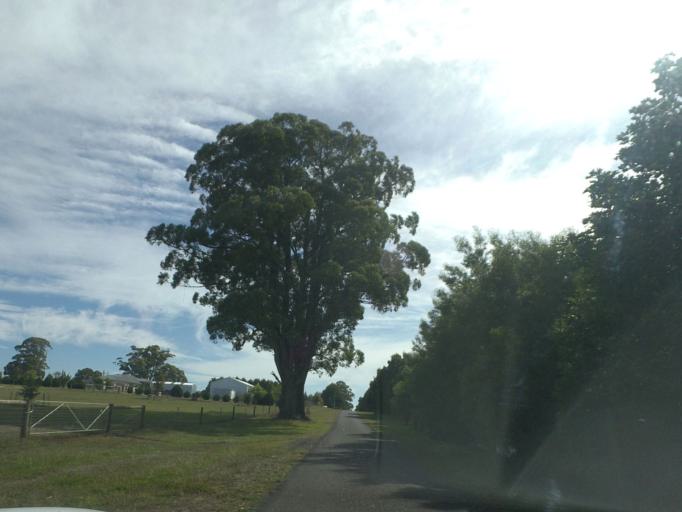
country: AU
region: Victoria
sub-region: Moorabool
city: Bacchus Marsh
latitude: -37.4008
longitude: 144.2545
